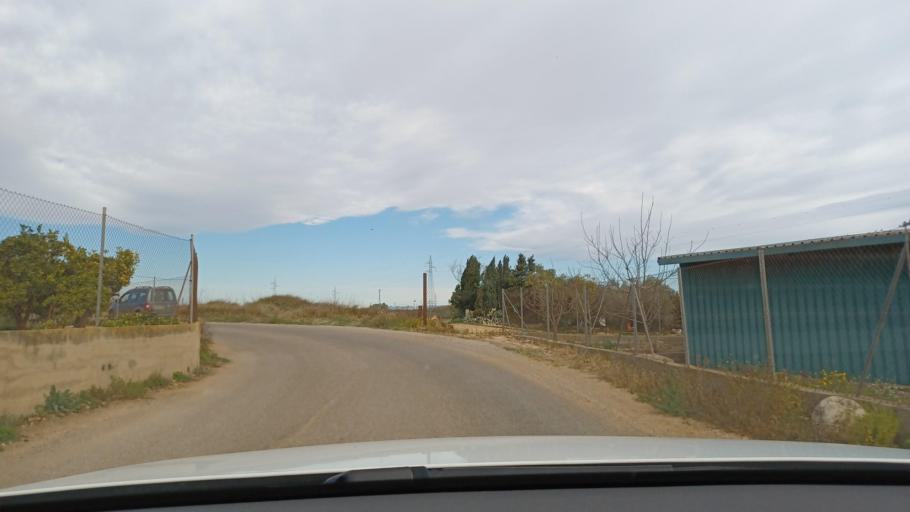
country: ES
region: Valencia
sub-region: Provincia de Valencia
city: Benifaio
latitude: 39.2901
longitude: -0.4348
